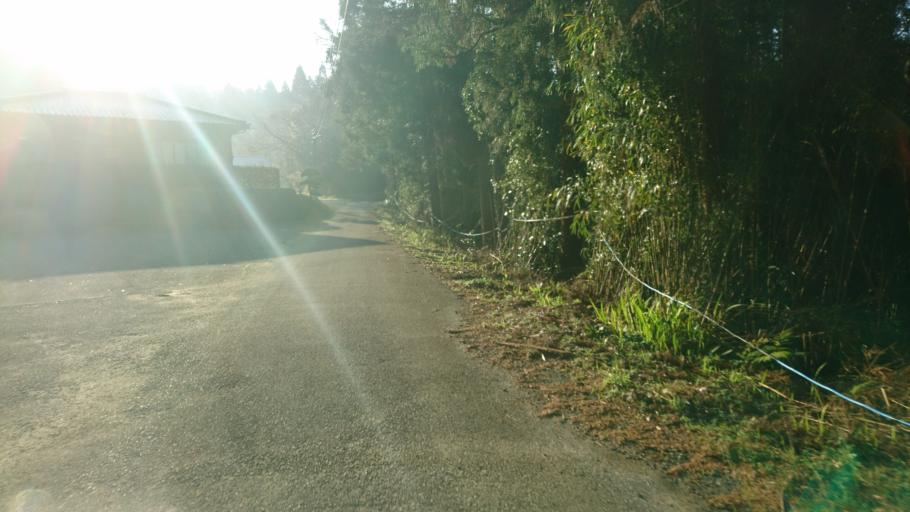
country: JP
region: Chiba
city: Kimitsu
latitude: 35.2857
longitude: 139.9567
